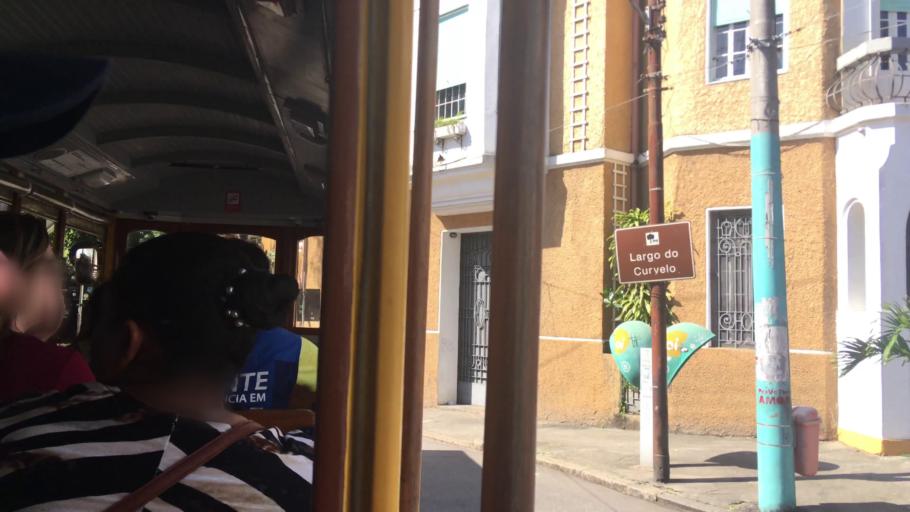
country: BR
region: Rio de Janeiro
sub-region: Rio De Janeiro
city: Rio de Janeiro
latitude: -22.9191
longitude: -43.1832
